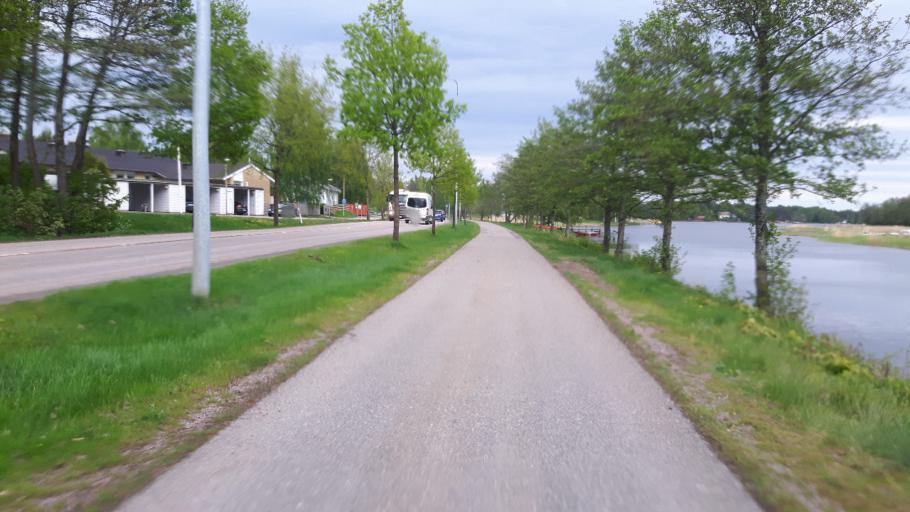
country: FI
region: Kymenlaakso
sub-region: Kotka-Hamina
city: Hamina
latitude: 60.5625
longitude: 27.2072
